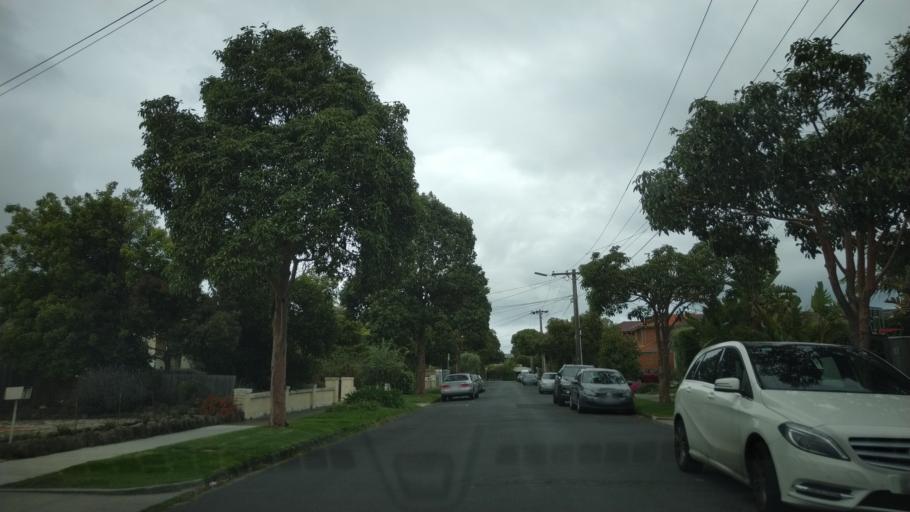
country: AU
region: Victoria
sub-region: Glen Eira
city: Caulfield South
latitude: -37.8884
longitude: 145.0274
